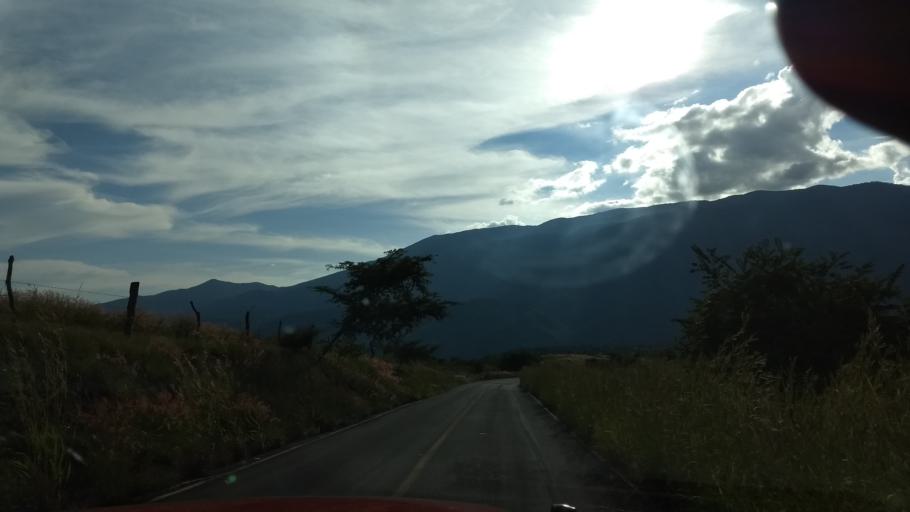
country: MX
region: Colima
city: Suchitlan
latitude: 19.4565
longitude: -103.8017
